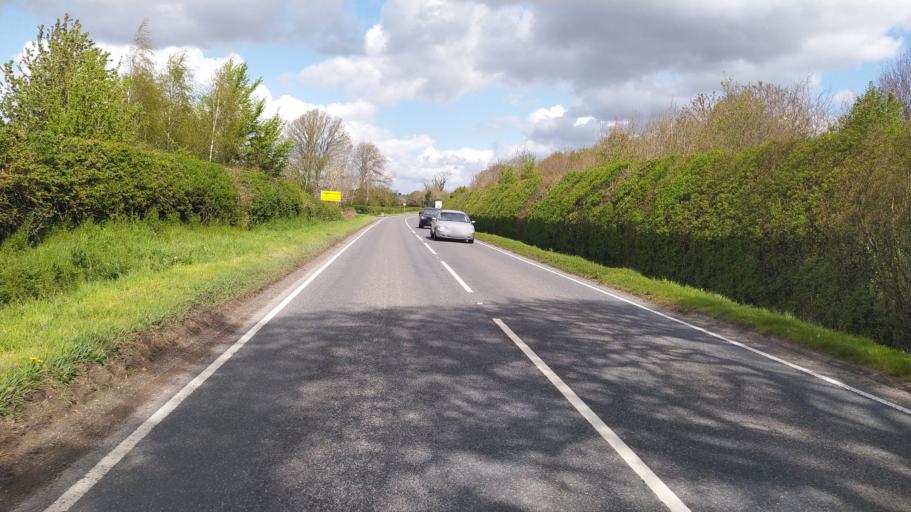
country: GB
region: England
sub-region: Somerset
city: Frome
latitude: 51.1859
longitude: -2.3152
